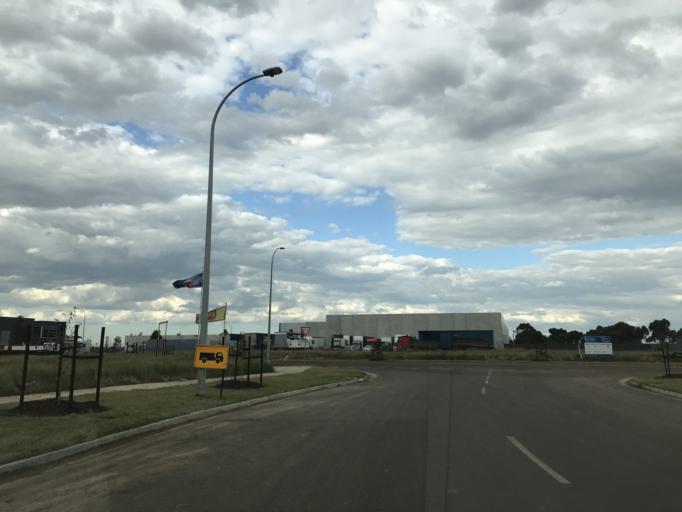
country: AU
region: Victoria
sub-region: Wyndham
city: Truganina
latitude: -37.8270
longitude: 144.7436
